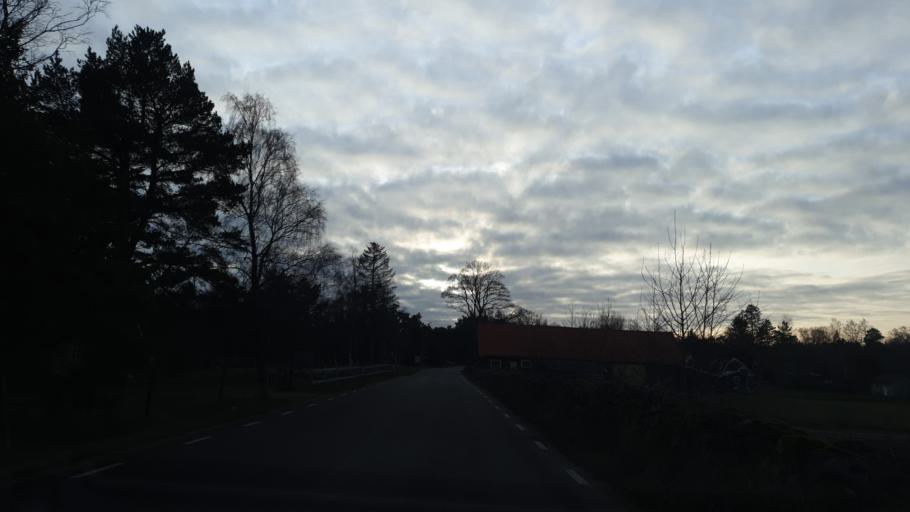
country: SE
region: Blekinge
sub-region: Karlskrona Kommun
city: Jaemjoe
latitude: 56.2124
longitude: 15.9680
